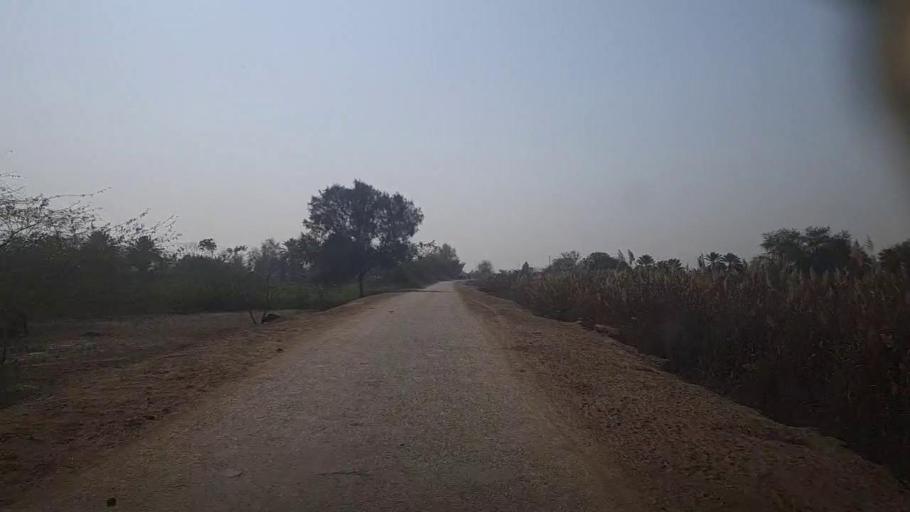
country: PK
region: Sindh
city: Kot Diji
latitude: 27.4139
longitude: 68.7942
